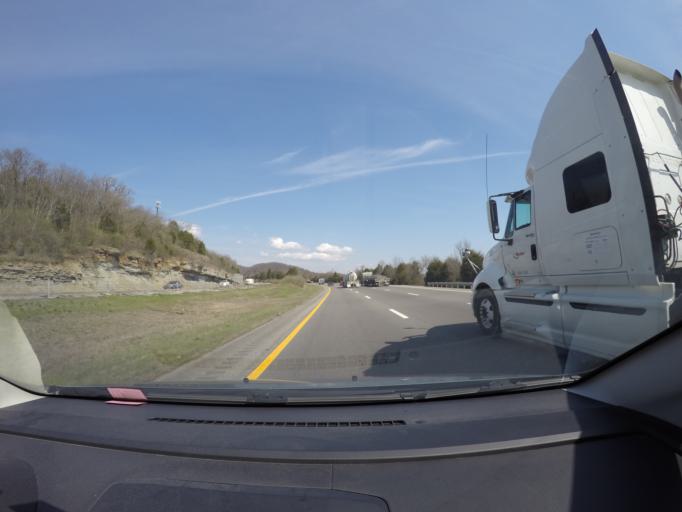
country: US
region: Tennessee
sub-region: Davidson County
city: Nashville
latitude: 36.2467
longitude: -86.7838
